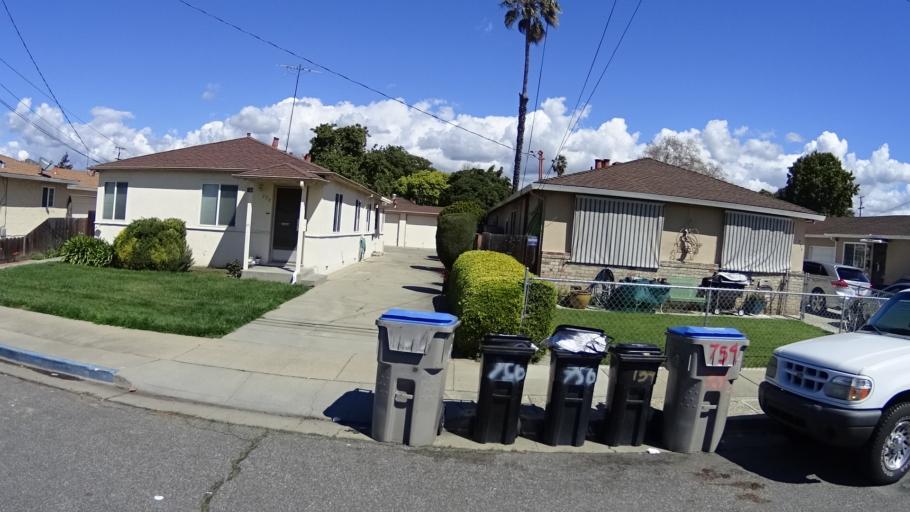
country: US
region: California
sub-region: Santa Clara County
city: San Jose
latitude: 37.3567
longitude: -121.8878
